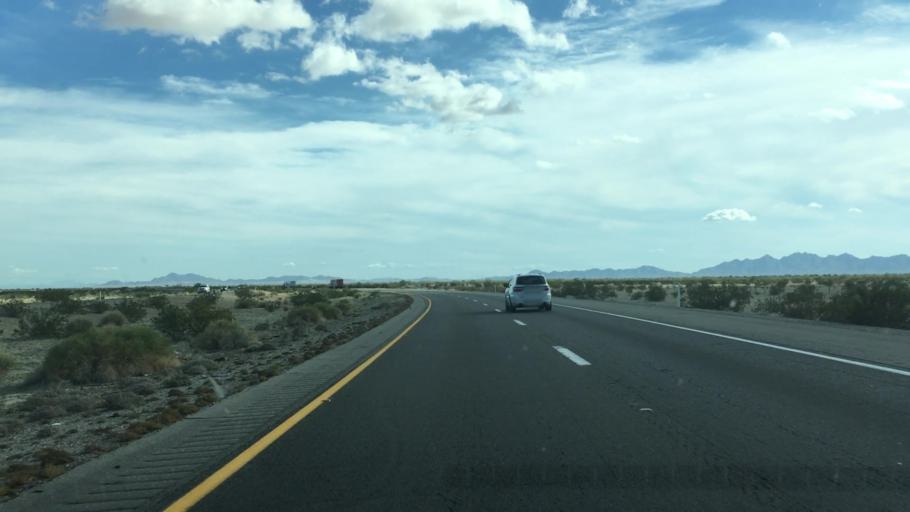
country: US
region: California
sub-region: Riverside County
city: Mesa Verde
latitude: 33.6323
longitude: -115.0771
